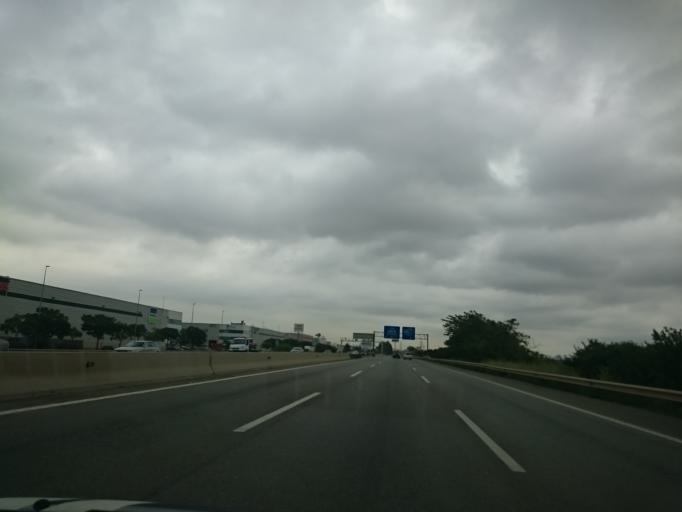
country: ES
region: Catalonia
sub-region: Provincia de Barcelona
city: Sant Boi de Llobregat
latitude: 41.3227
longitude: 2.0430
